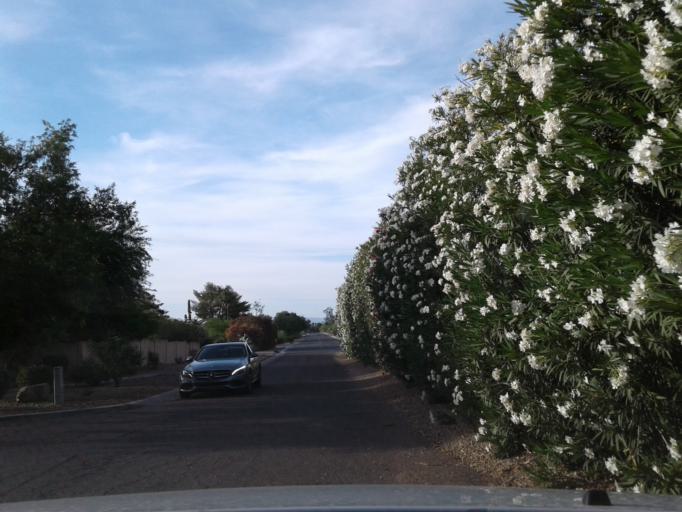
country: US
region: Arizona
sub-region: Maricopa County
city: Paradise Valley
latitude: 33.5581
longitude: -111.9606
